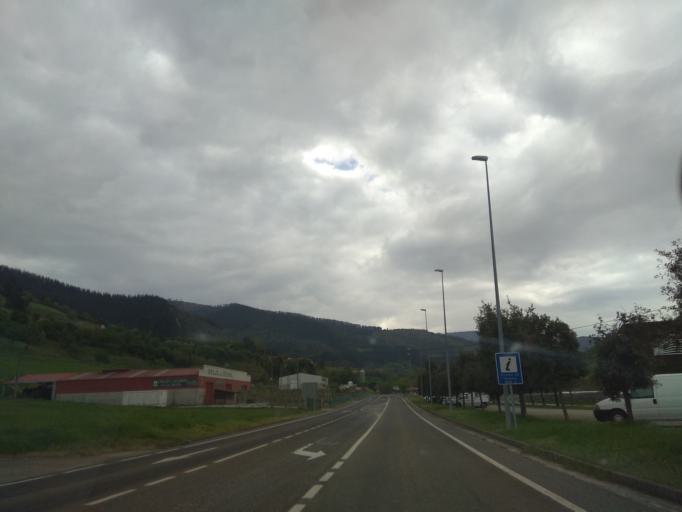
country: ES
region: Cantabria
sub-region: Provincia de Cantabria
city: Potes
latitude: 43.1829
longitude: -4.6014
